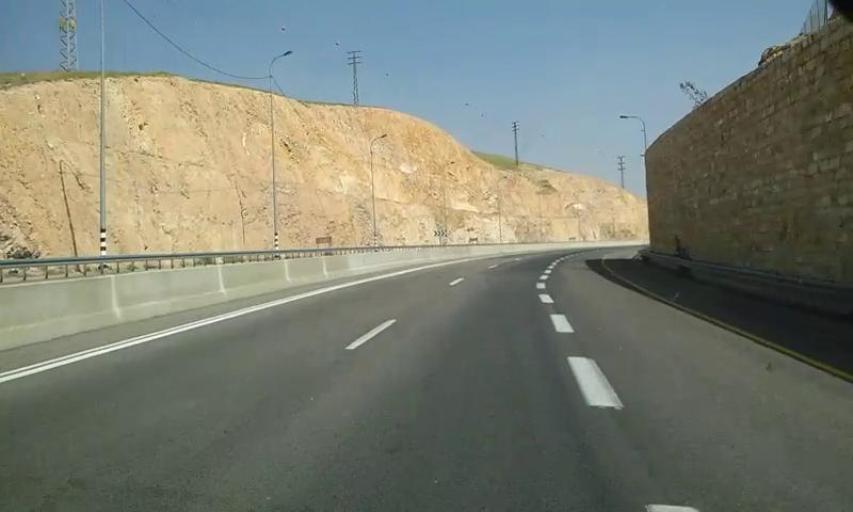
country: PS
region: West Bank
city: Hizma
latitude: 31.8173
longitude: 35.3596
